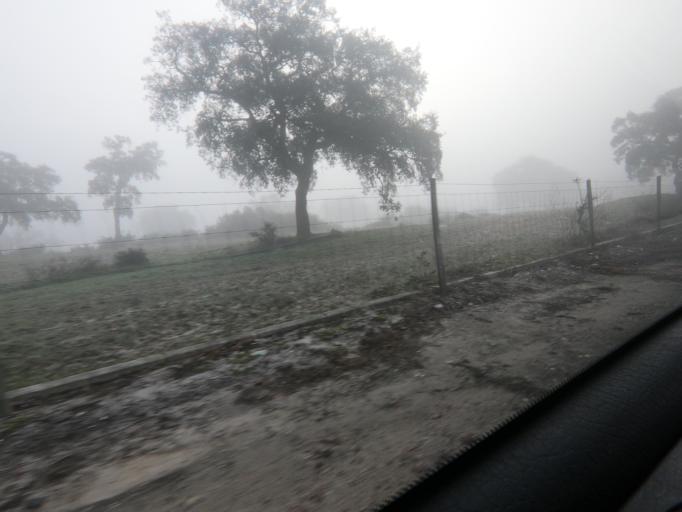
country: PT
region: Setubal
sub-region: Palmela
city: Palmela
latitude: 38.5765
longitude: -8.8327
